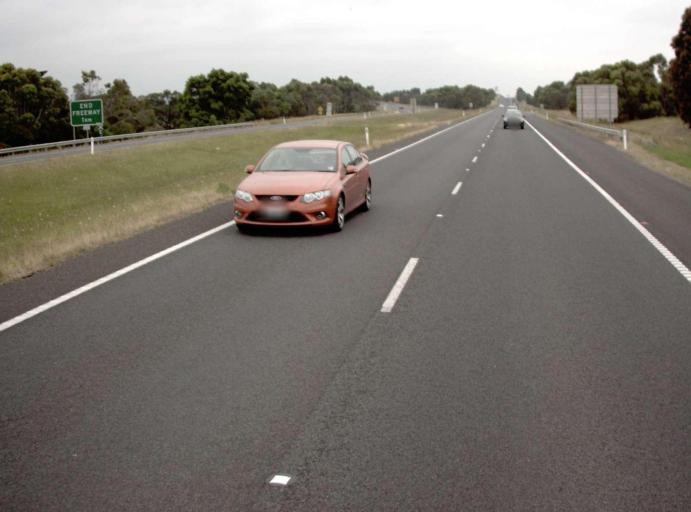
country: AU
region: Victoria
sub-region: Latrobe
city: Morwell
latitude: -38.2355
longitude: 146.4532
